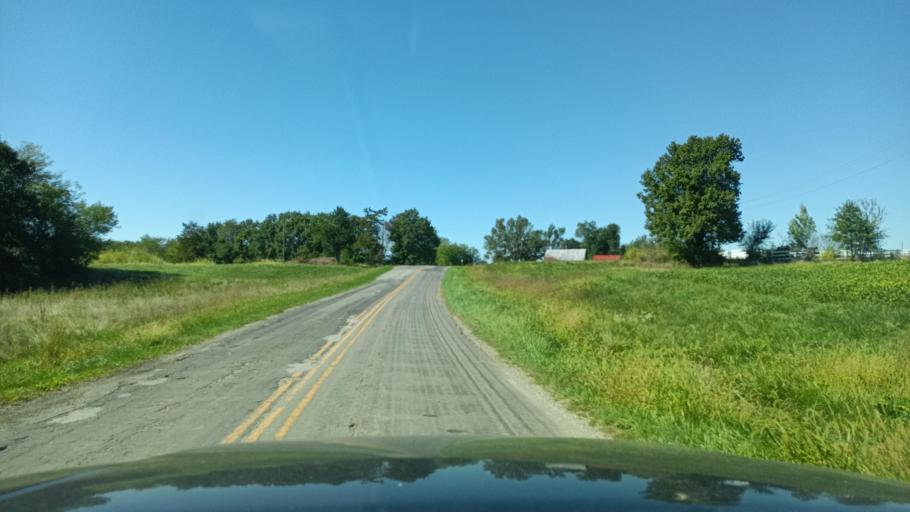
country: US
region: Missouri
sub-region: Scotland County
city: Memphis
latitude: 40.3525
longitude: -92.3043
